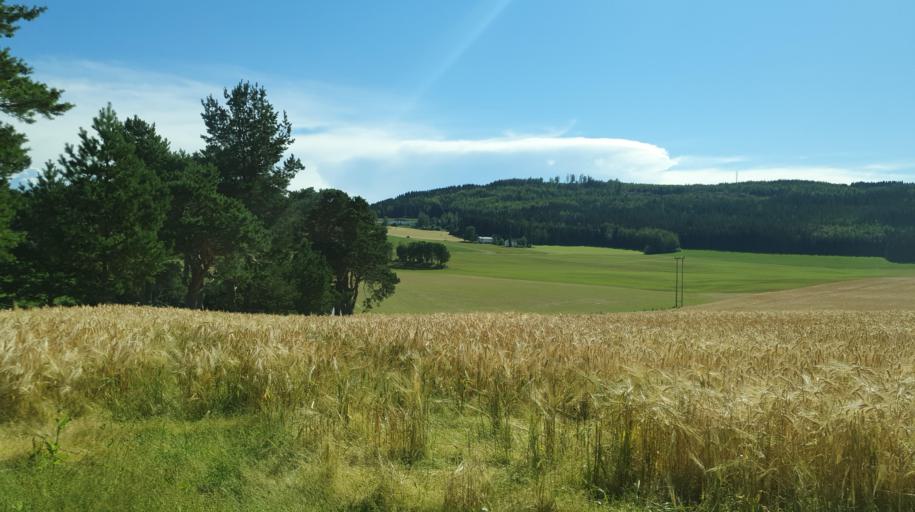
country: NO
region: Nord-Trondelag
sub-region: Verdal
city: Verdal
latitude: 63.7767
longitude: 11.3977
